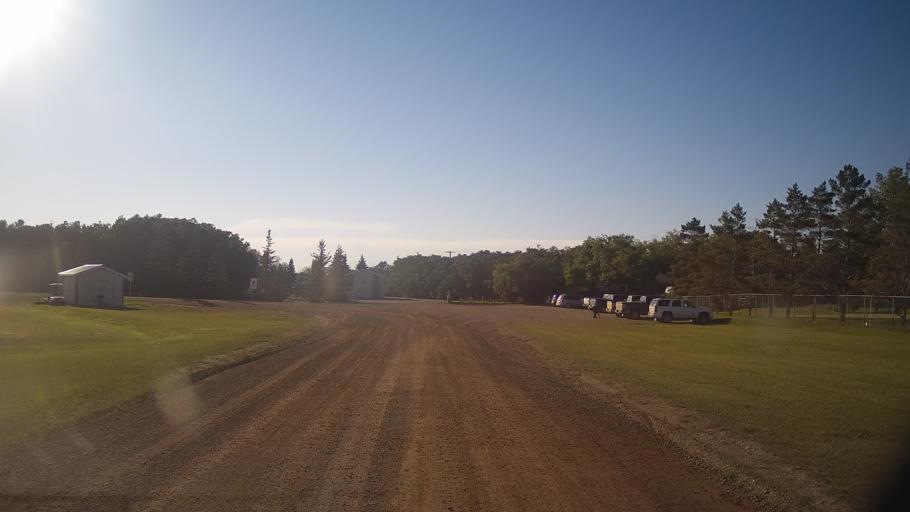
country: CA
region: Saskatchewan
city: Lanigan
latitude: 51.8507
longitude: -105.0171
